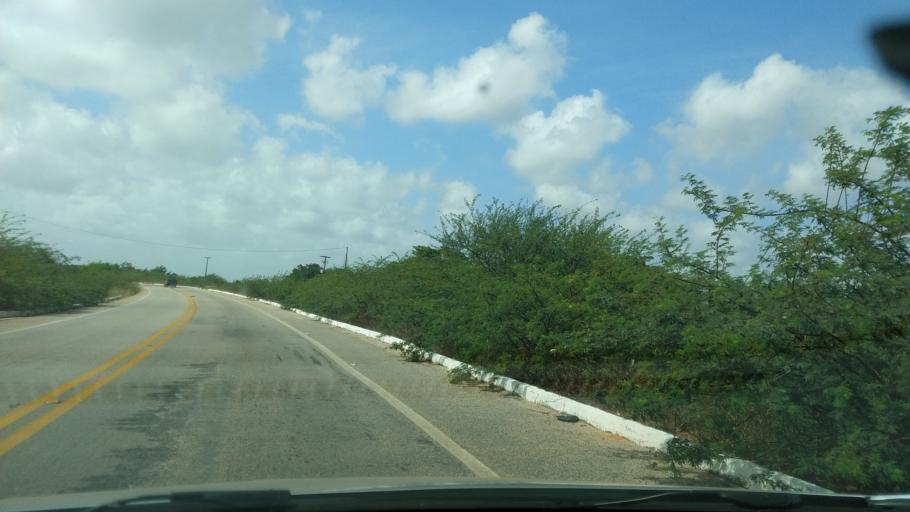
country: BR
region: Rio Grande do Norte
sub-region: Touros
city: Touros
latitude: -5.1819
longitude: -35.5116
